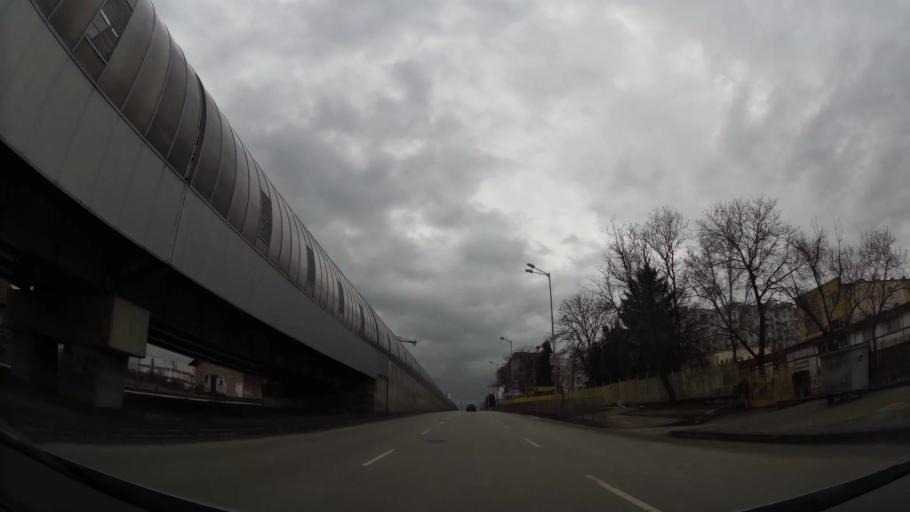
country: BG
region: Sofia-Capital
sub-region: Stolichna Obshtina
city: Sofia
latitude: 42.7396
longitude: 23.2881
